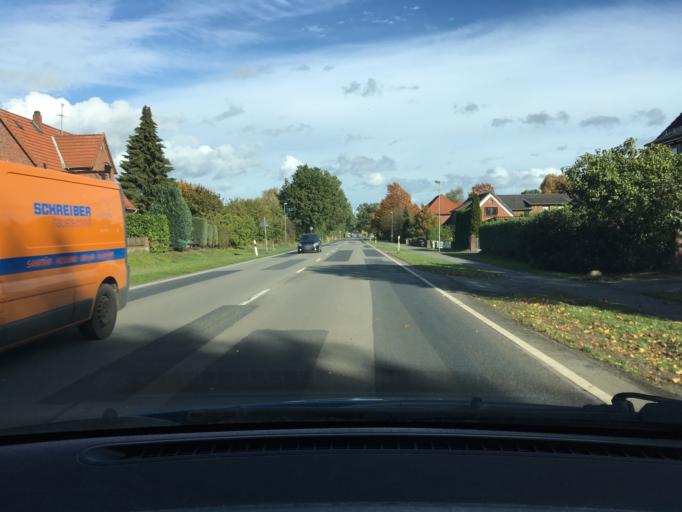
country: DE
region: Lower Saxony
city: Wistedt
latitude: 53.2666
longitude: 9.6750
